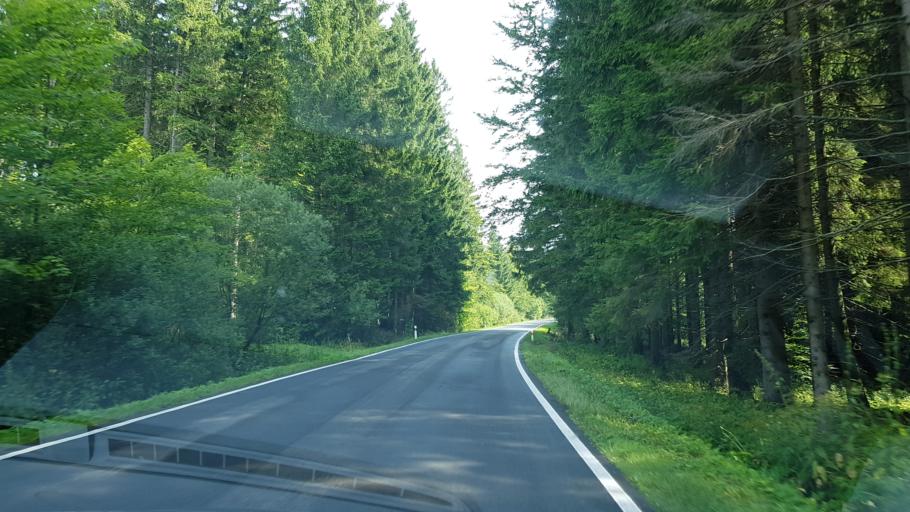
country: CZ
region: Olomoucky
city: Pisecna
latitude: 50.2250
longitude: 17.2748
